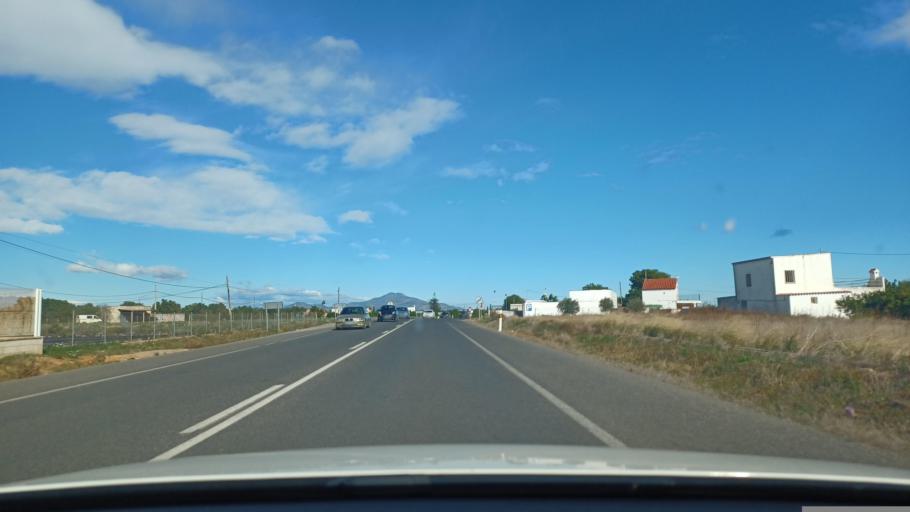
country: ES
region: Valencia
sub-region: Provincia de Castello
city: Benicarlo
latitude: 40.4380
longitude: 0.4409
